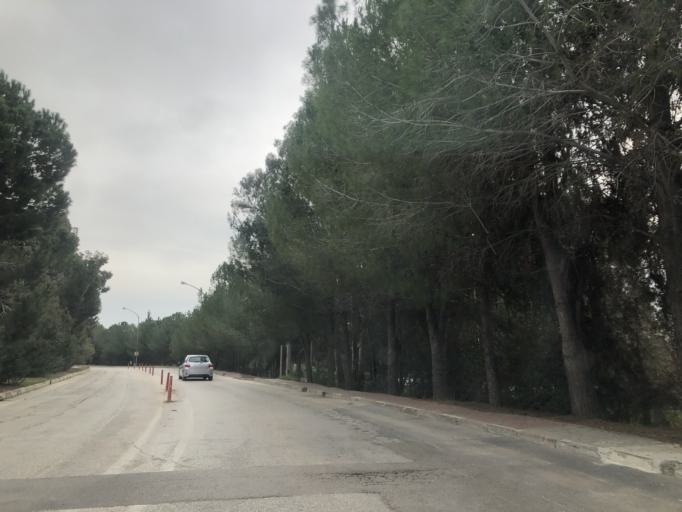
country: TR
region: Adana
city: Adana
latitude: 37.0564
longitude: 35.3544
